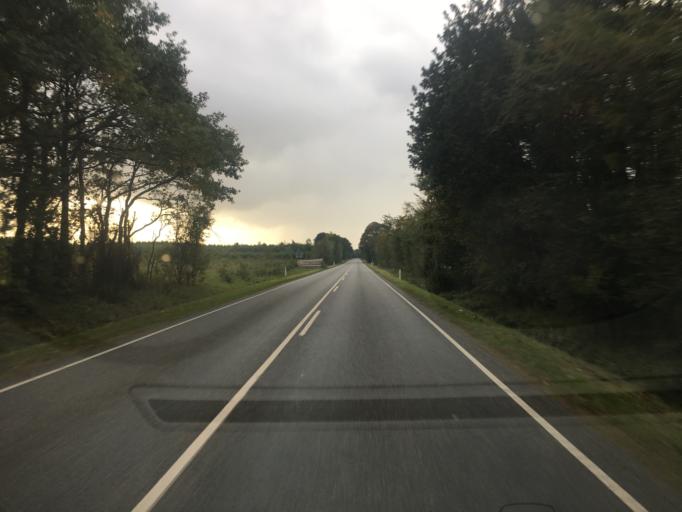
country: DK
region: South Denmark
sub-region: Tonder Kommune
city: Logumkloster
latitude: 55.0603
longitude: 8.9173
